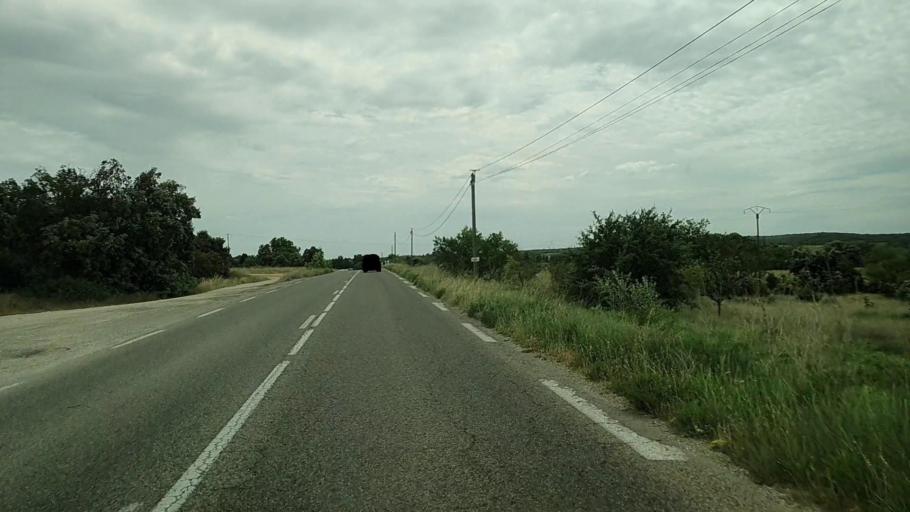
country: FR
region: Languedoc-Roussillon
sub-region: Departement du Gard
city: Connaux
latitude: 44.0484
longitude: 4.5737
